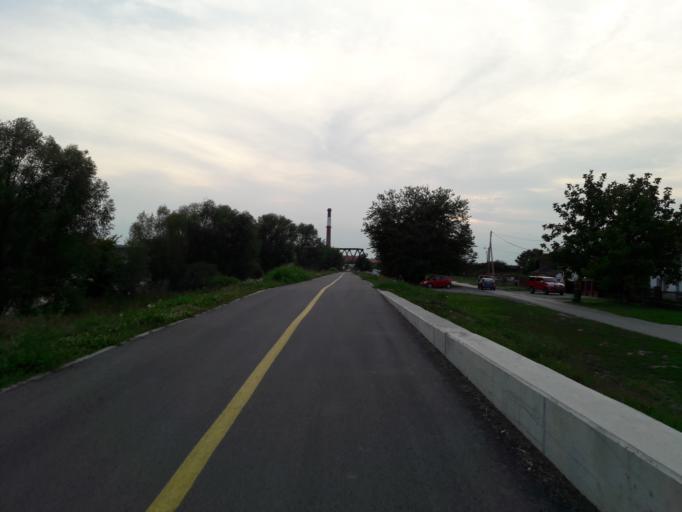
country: HR
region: Osjecko-Baranjska
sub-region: Grad Osijek
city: Osijek
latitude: 45.5615
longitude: 18.7086
